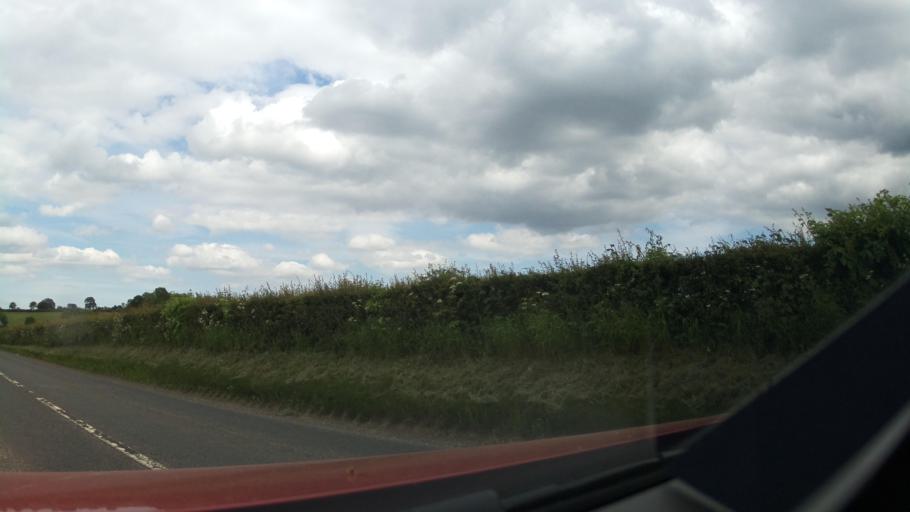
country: GB
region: England
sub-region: Herefordshire
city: Yatton
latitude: 51.9715
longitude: -2.5194
